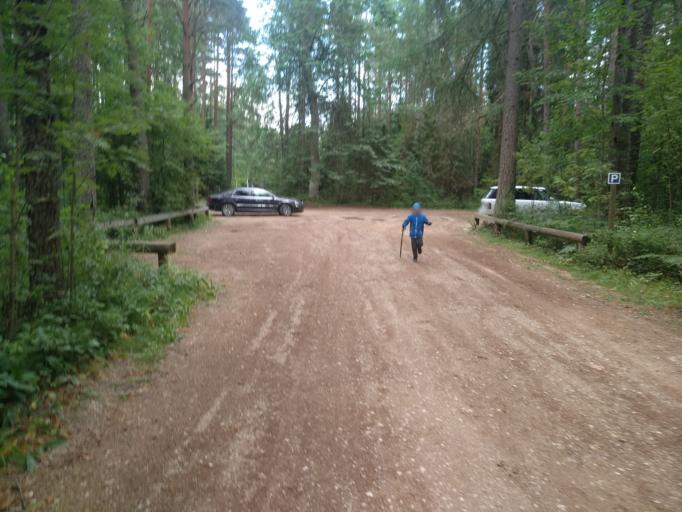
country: EE
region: Harju
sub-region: Anija vald
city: Kehra
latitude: 59.1887
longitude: 25.5096
